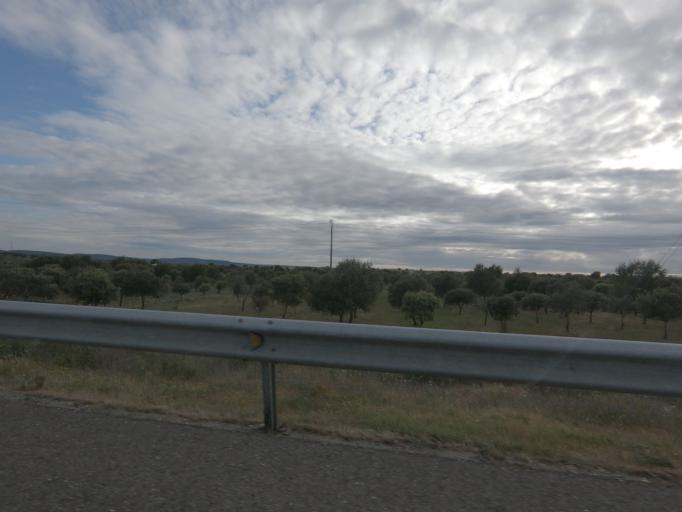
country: ES
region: Extremadura
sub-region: Provincia de Caceres
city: Torrejoncillo
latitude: 39.9287
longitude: -6.5029
